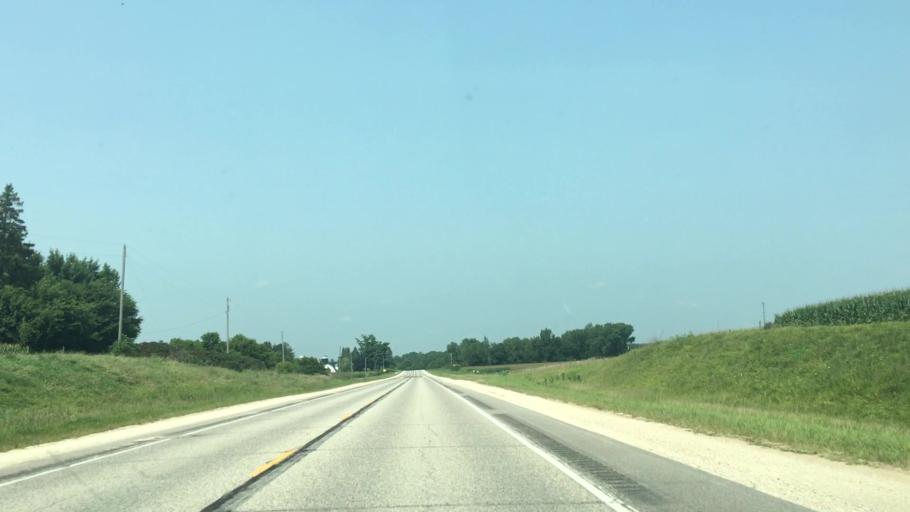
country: US
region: Iowa
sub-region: Fayette County
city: Fayette
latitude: 42.8209
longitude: -91.8050
